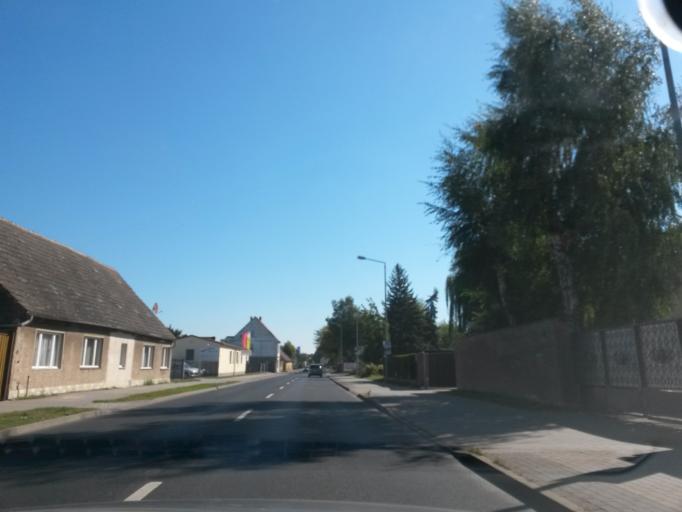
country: DE
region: Brandenburg
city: Prenzlau
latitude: 53.3083
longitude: 13.8368
